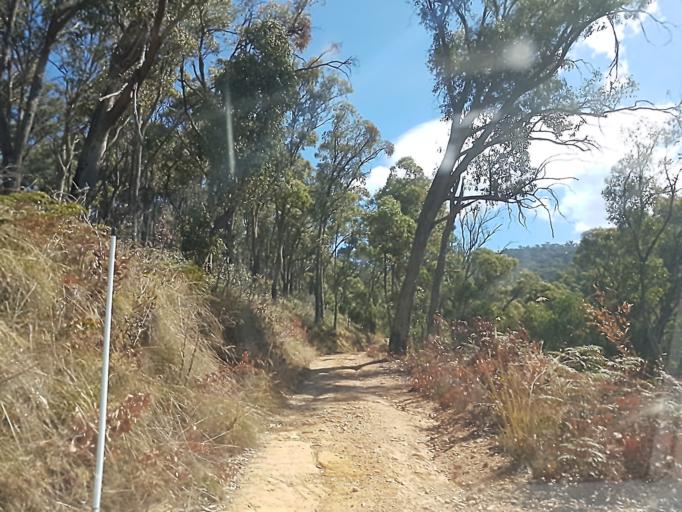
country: AU
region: Victoria
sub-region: Alpine
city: Mount Beauty
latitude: -36.8807
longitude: 147.0386
